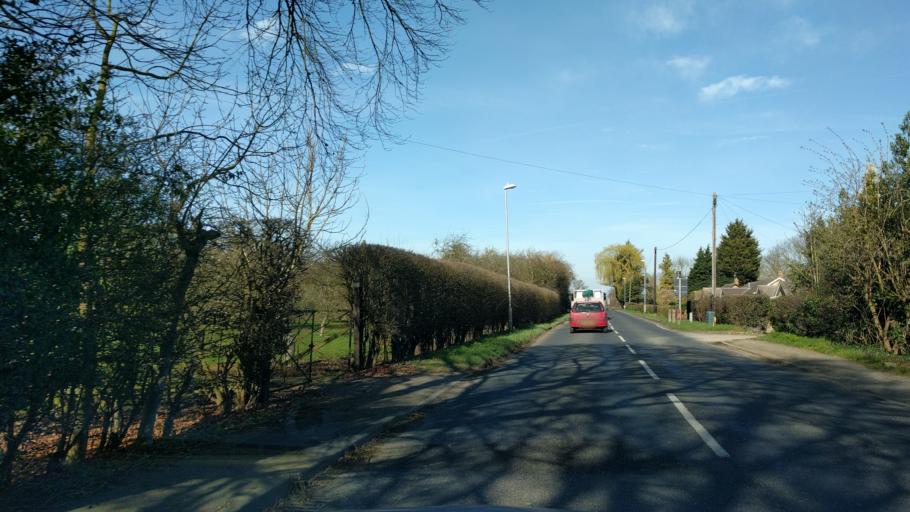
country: GB
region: England
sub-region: Cambridgeshire
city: Earith
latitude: 52.3194
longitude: 0.0598
